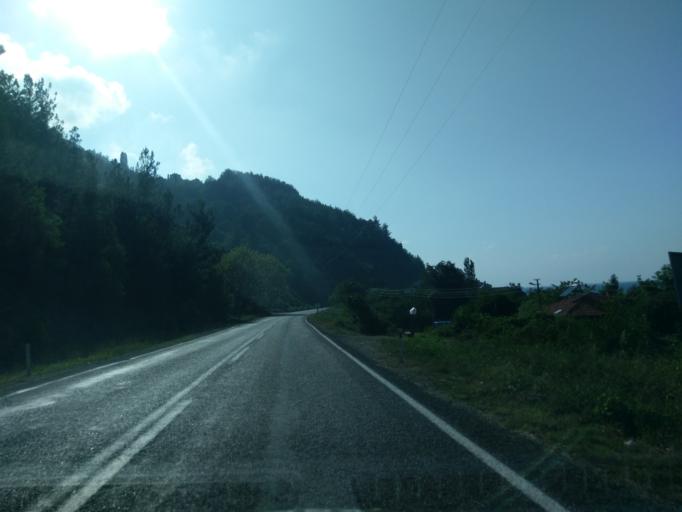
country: TR
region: Sinop
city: Ayancik
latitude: 41.9406
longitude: 34.6484
